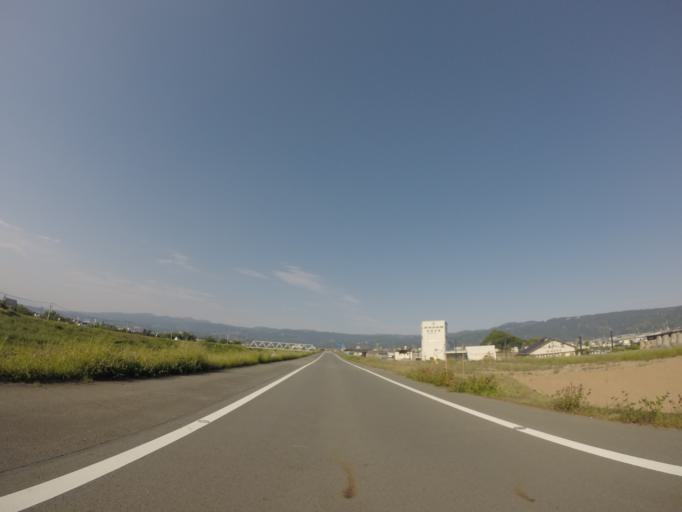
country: JP
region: Shizuoka
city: Mishima
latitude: 35.0764
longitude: 138.9244
